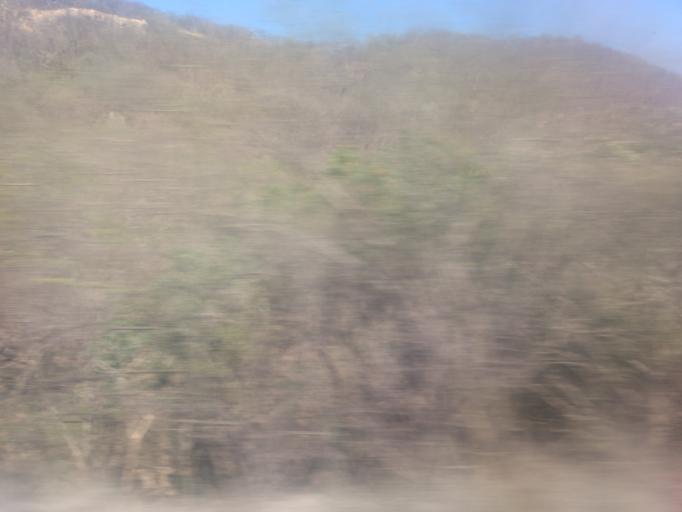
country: MX
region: Colima
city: El Colomo
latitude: 19.0027
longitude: -104.2433
